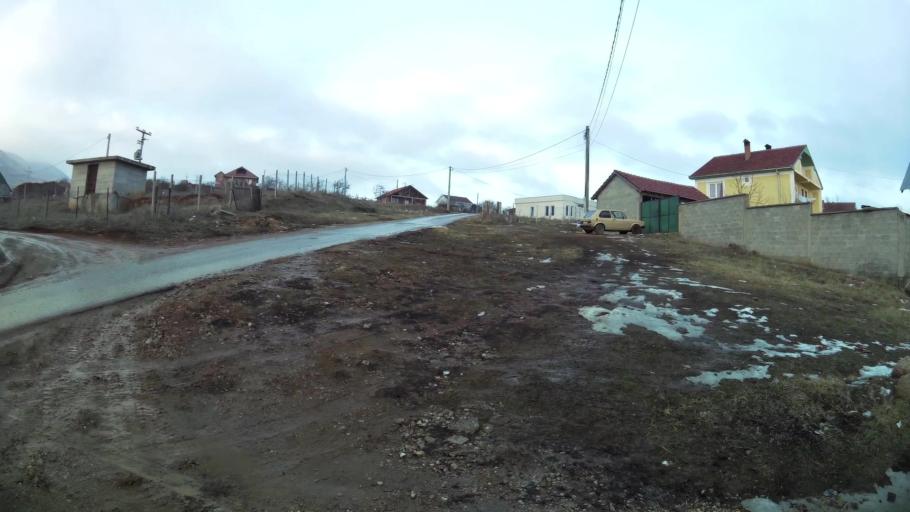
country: MK
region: Aracinovo
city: Arachinovo
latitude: 42.0300
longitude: 21.5784
